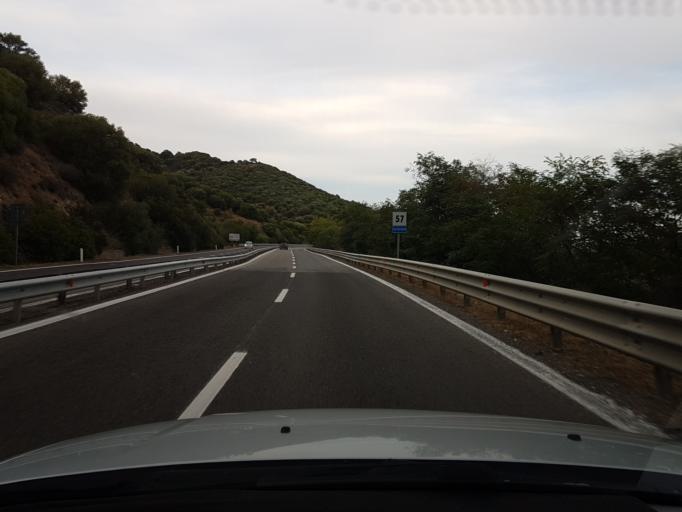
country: IT
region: Sardinia
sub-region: Provincia di Nuoro
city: Nuoro
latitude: 40.3543
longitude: 9.3444
